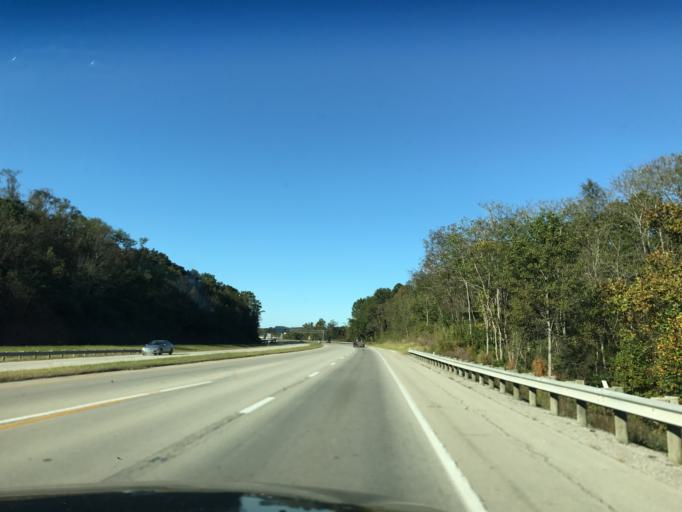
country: US
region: West Virginia
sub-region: Wood County
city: Washington
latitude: 39.2830
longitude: -81.6779
